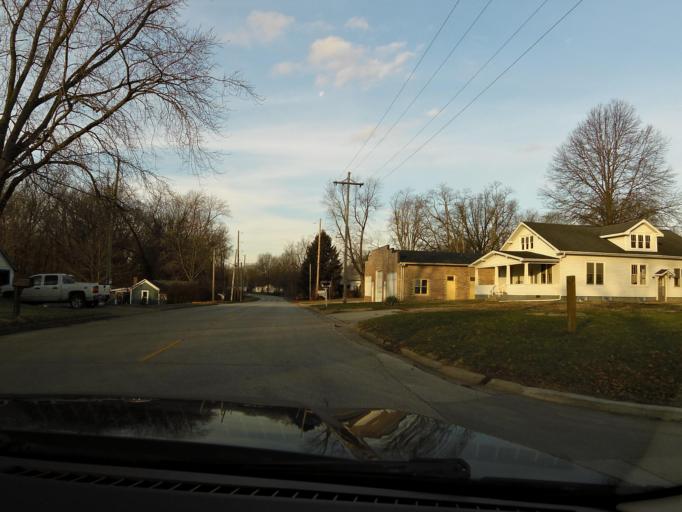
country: US
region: Illinois
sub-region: Fayette County
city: Vandalia
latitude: 38.9576
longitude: -89.1119
